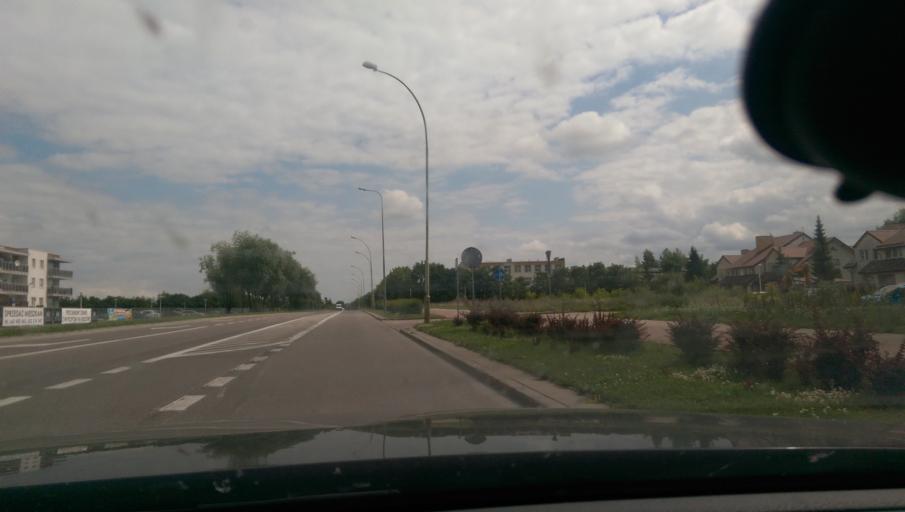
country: PL
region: Podlasie
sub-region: Suwalki
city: Suwalki
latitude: 54.1042
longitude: 22.9077
